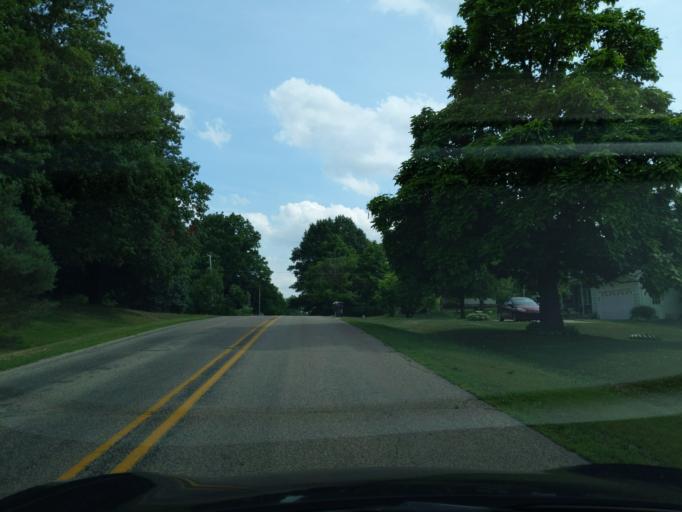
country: US
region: Michigan
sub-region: Eaton County
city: Eaton Rapids
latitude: 42.5528
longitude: -84.6020
